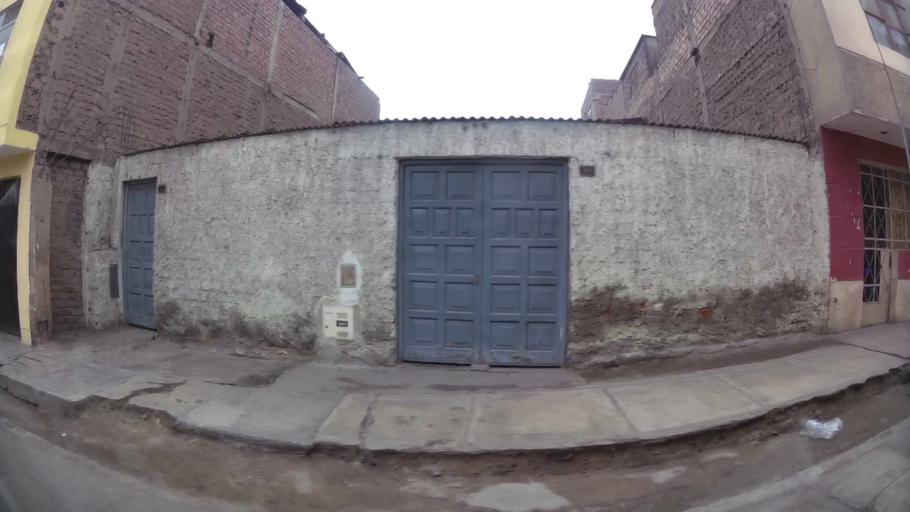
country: PE
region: Lima
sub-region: Lima
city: Surco
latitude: -12.1569
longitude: -76.9610
